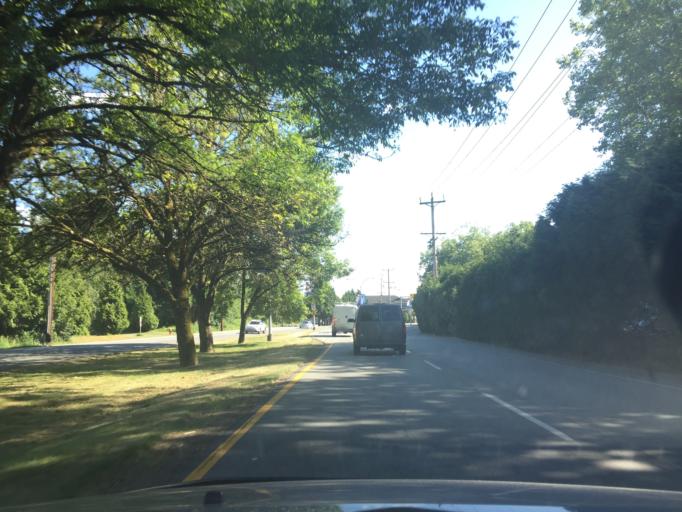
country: CA
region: British Columbia
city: Richmond
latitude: 49.1650
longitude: -123.1248
